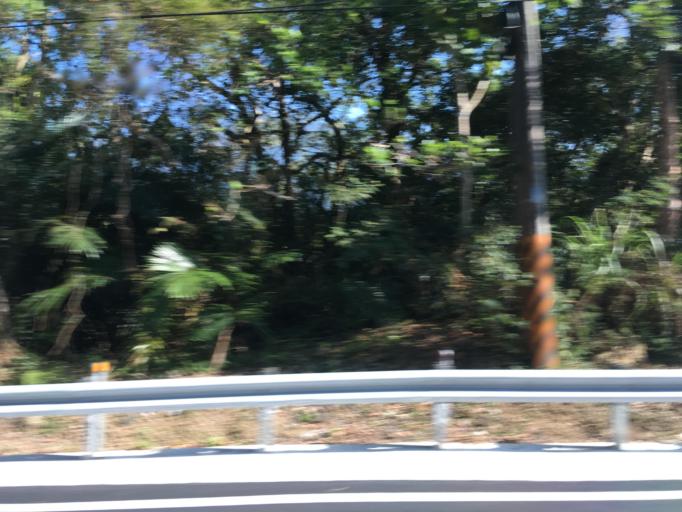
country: TW
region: Taiwan
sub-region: Chiayi
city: Jiayi Shi
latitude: 23.4360
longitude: 120.6235
